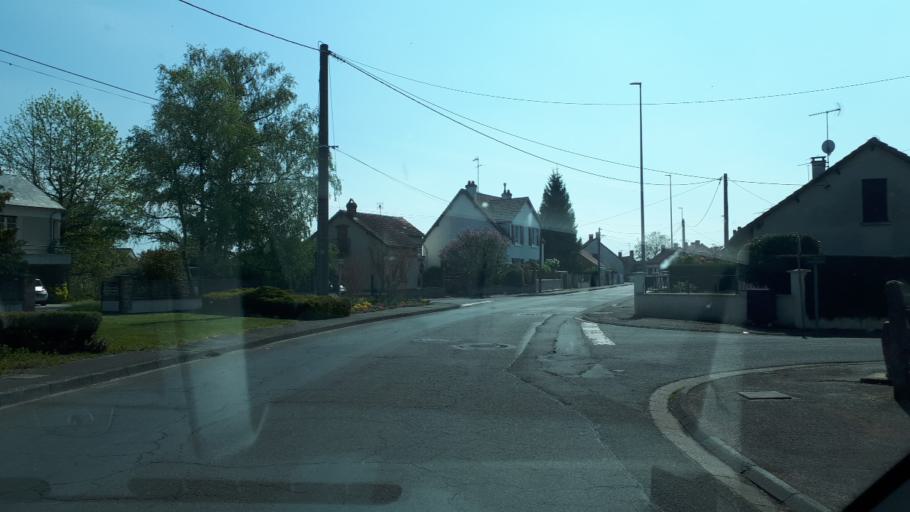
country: FR
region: Centre
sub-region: Departement du Loir-et-Cher
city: Romorantin-Lanthenay
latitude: 47.3605
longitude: 1.7502
